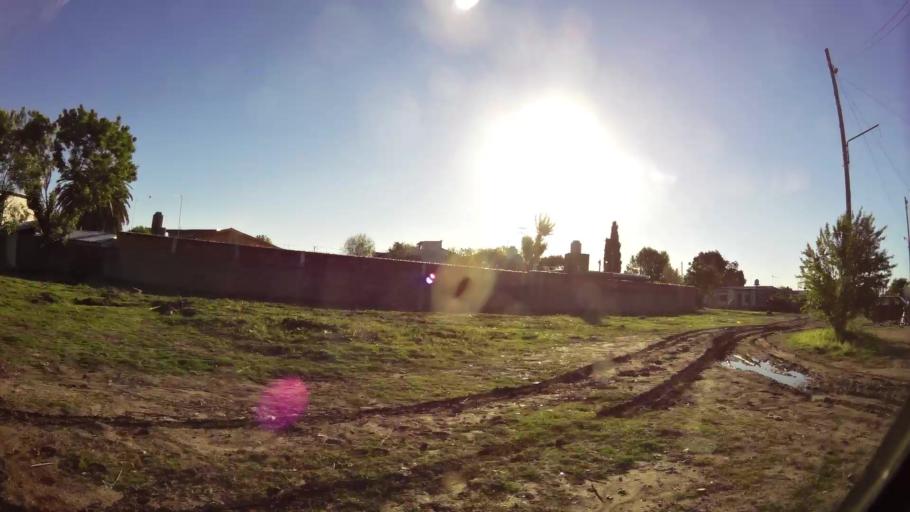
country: AR
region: Buenos Aires
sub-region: Partido de Almirante Brown
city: Adrogue
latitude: -34.7648
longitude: -58.3335
